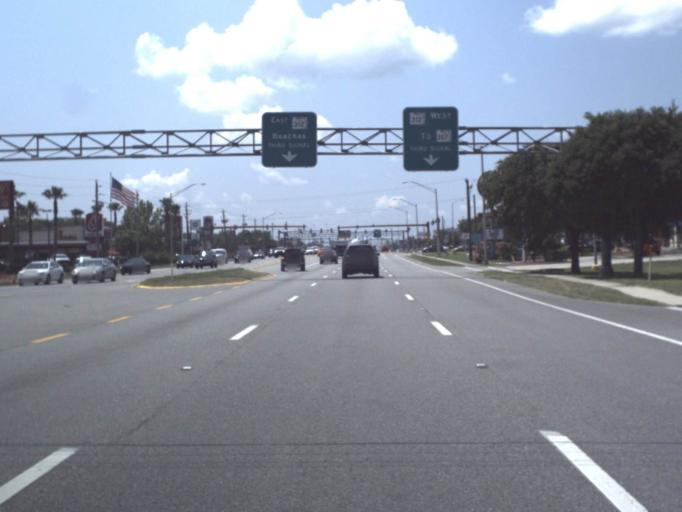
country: US
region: Florida
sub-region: Saint Johns County
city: Saint Augustine
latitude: 29.8710
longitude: -81.3233
